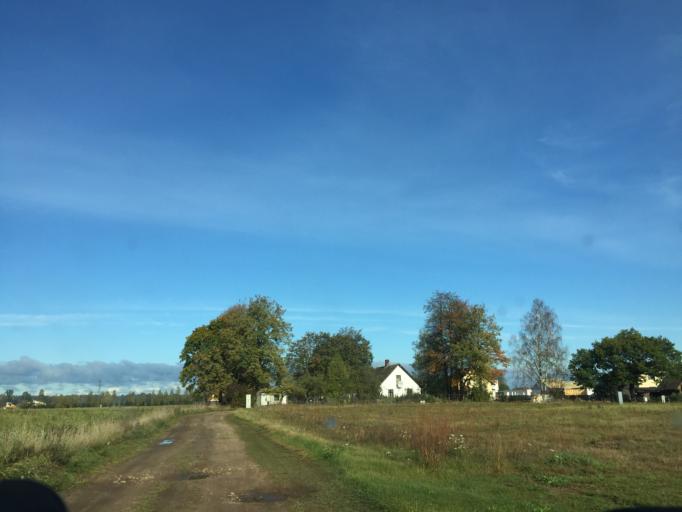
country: LV
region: Adazi
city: Adazi
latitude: 57.0886
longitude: 24.3062
